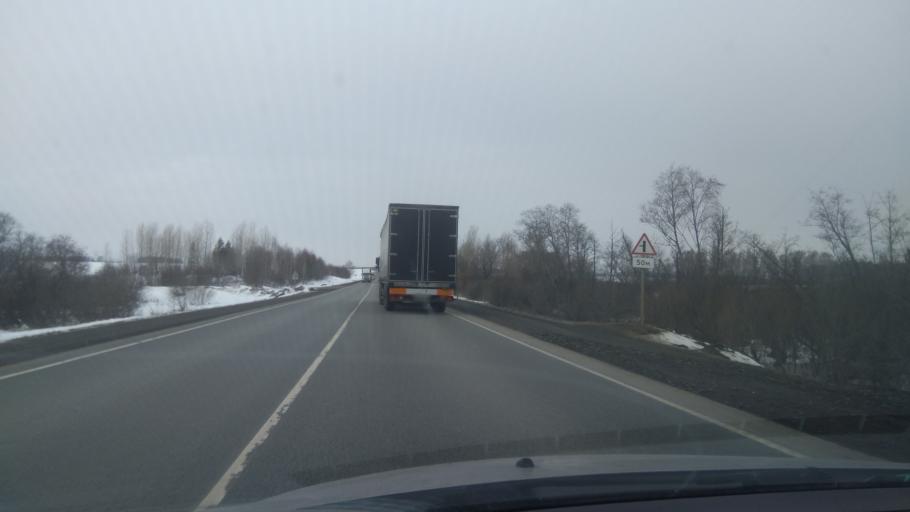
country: RU
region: Sverdlovsk
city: Ufimskiy
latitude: 56.7711
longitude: 58.0851
